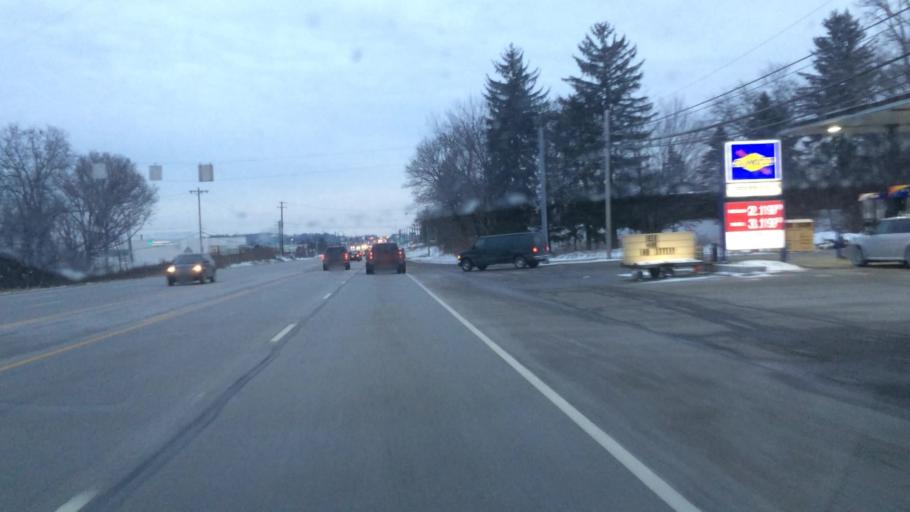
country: US
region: Ohio
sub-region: Summit County
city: Montrose-Ghent
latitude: 41.1359
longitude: -81.6661
